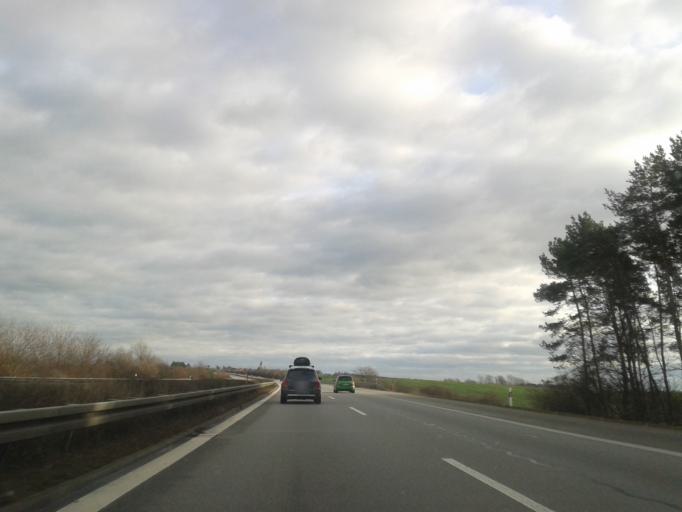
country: DE
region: Saxony
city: Hochkirch
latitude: 51.2083
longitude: 14.5914
